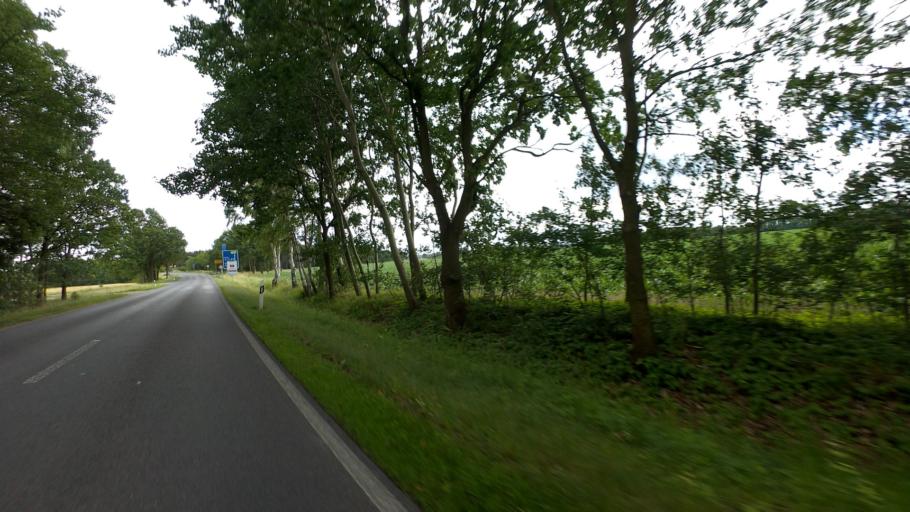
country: DE
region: Brandenburg
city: Calau
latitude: 51.7872
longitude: 13.8718
